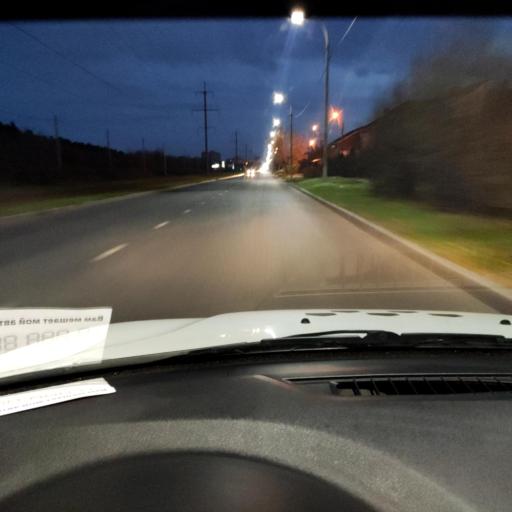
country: RU
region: Samara
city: Tol'yatti
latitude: 53.5173
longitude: 49.3955
